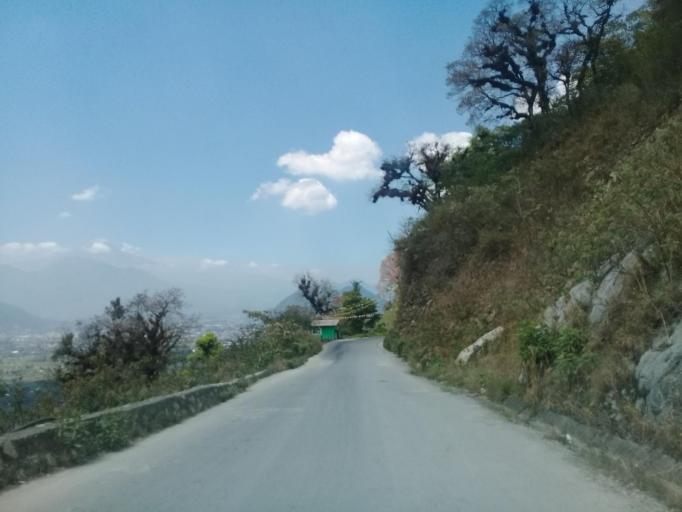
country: MX
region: Veracruz
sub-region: Tlilapan
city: Tonalixco
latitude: 18.8078
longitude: -97.0605
